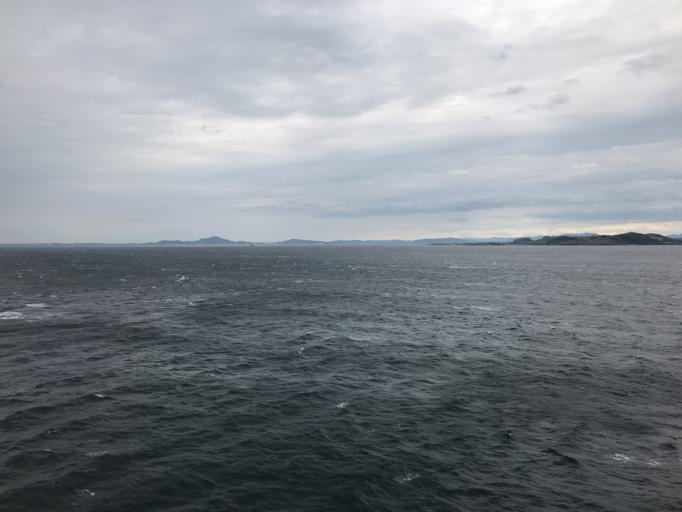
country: NO
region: Rogaland
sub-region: Randaberg
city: Randaberg
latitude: 59.0508
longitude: 5.5607
